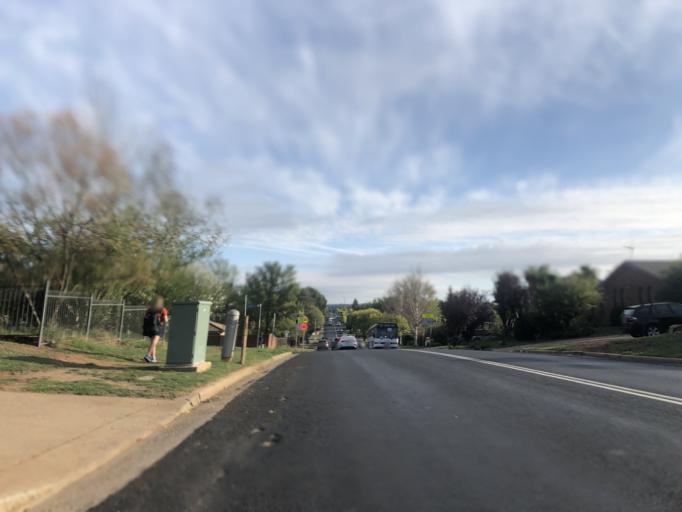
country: AU
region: New South Wales
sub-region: Orange Municipality
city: Orange
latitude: -33.3034
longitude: 149.0948
